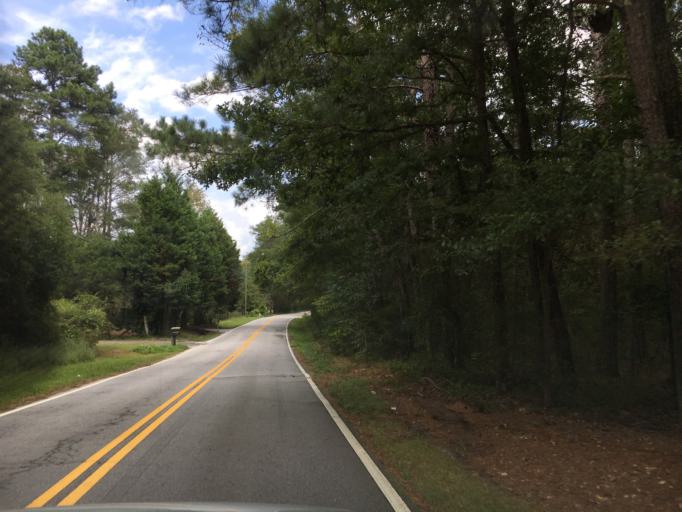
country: US
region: Georgia
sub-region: Rockdale County
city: Lakeview Estates
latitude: 33.7022
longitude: -84.0289
